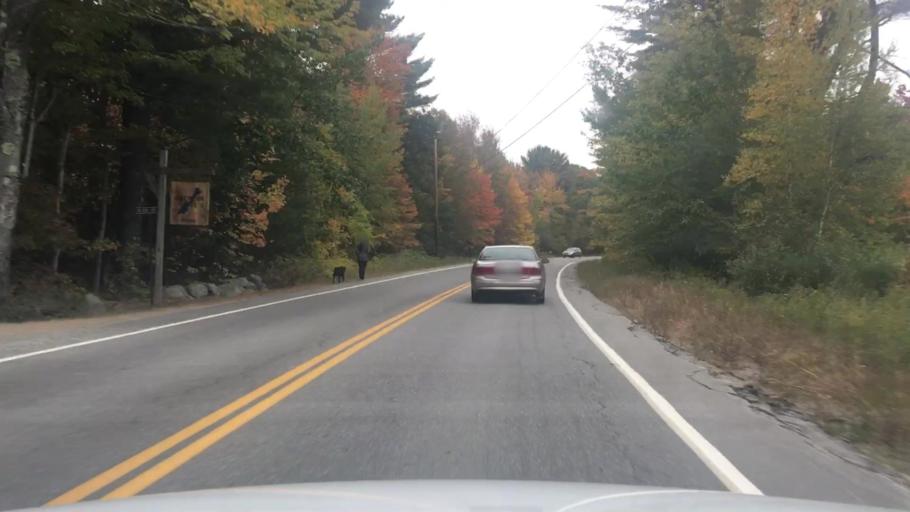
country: US
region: Maine
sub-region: Kennebec County
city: Oakland
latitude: 44.5408
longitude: -69.7930
